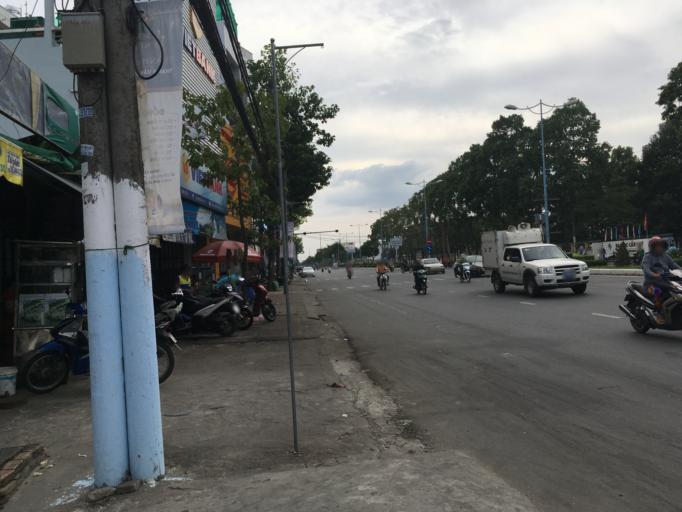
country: VN
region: Can Tho
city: Can Tho
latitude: 10.0304
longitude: 105.7727
